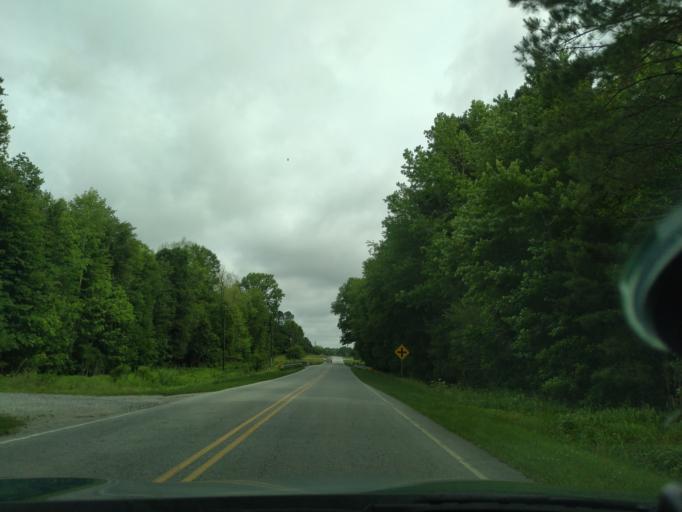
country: US
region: North Carolina
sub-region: Washington County
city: Plymouth
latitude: 35.8483
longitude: -76.7318
